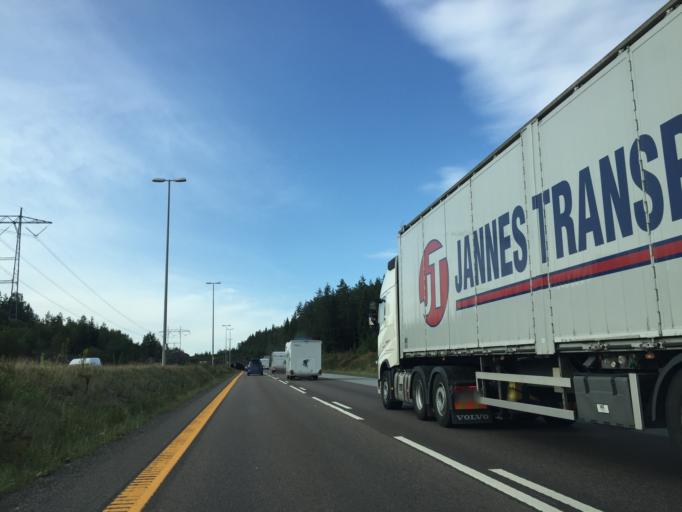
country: NO
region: Akershus
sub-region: Oppegard
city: Kolbotn
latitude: 59.7933
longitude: 10.8412
